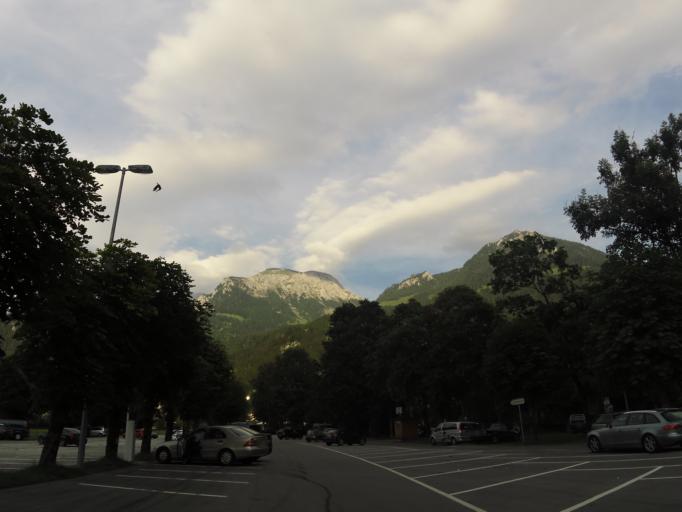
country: DE
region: Bavaria
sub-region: Upper Bavaria
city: Schoenau am Koenigssee
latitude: 47.5913
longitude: 12.9894
